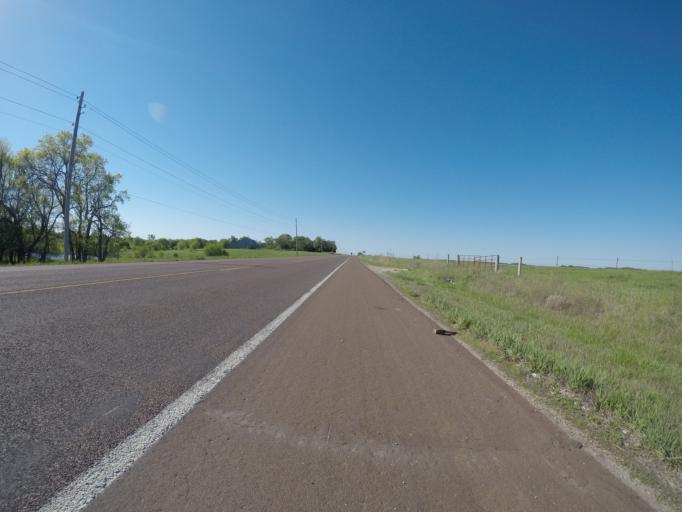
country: US
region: Kansas
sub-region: Douglas County
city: Lawrence
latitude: 39.0297
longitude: -95.3913
